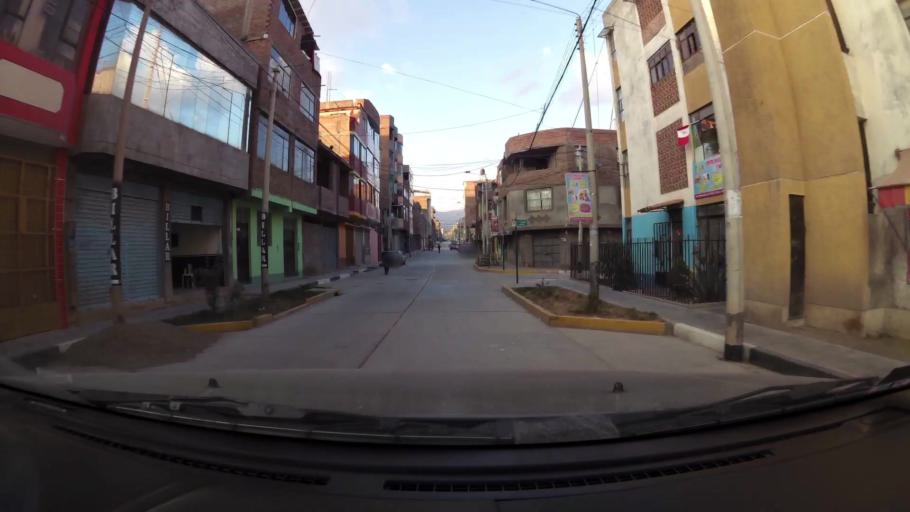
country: PE
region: Junin
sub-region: Provincia de Huancayo
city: Pilcomay
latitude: -12.0465
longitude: -75.2303
